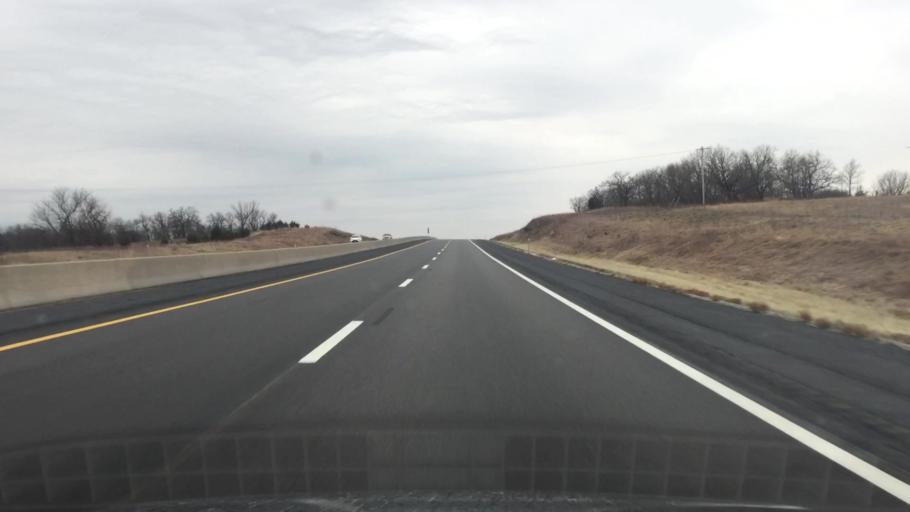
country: US
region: Kansas
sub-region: Shawnee County
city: Auburn
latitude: 38.7838
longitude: -95.9165
